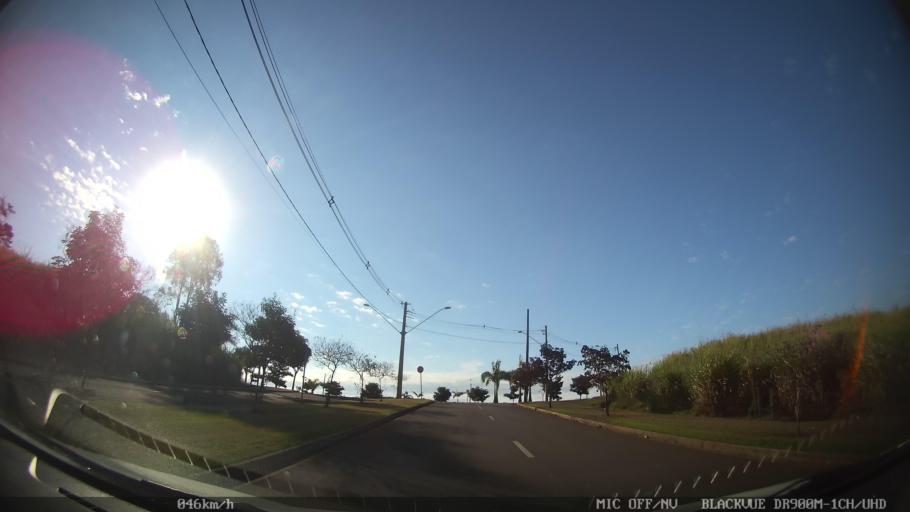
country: BR
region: Sao Paulo
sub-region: Piracicaba
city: Piracicaba
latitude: -22.6926
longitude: -47.6155
